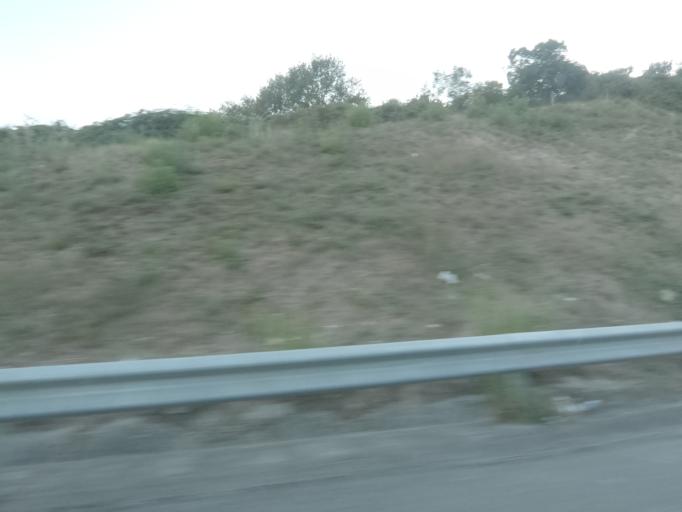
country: PT
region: Vila Real
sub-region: Peso da Regua
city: Peso da Regua
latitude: 41.1693
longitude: -7.7746
